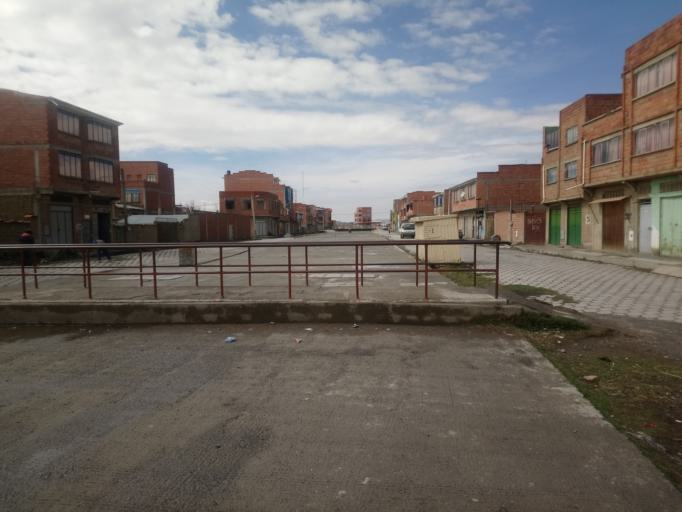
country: BO
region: La Paz
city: Achacachi
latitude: -16.0474
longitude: -68.6850
